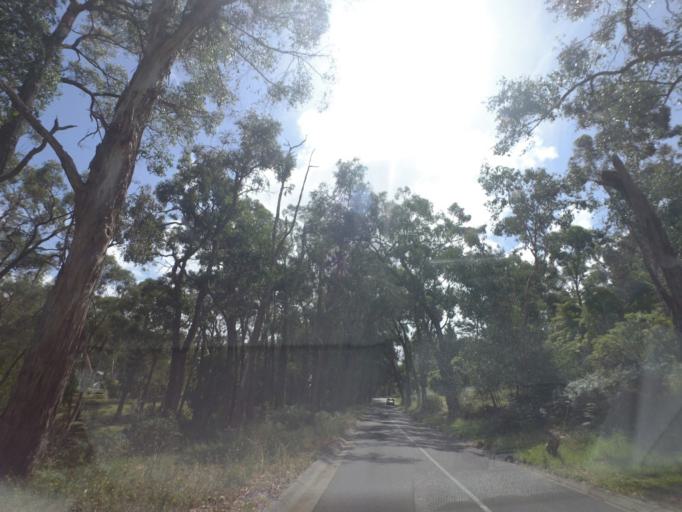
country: AU
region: Victoria
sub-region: Yarra Ranges
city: Montrose
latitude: -37.7944
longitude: 145.3550
